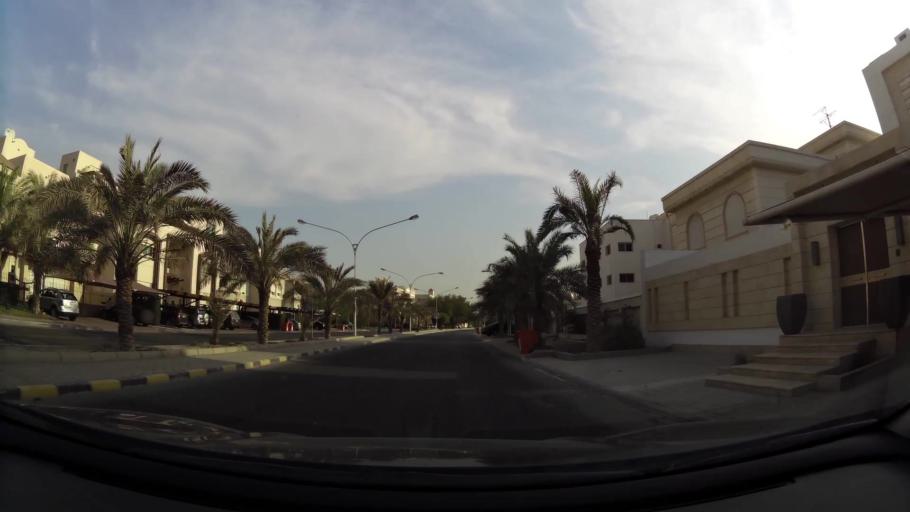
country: KW
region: Muhafazat Hawalli
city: Hawalli
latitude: 29.3097
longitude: 48.0145
